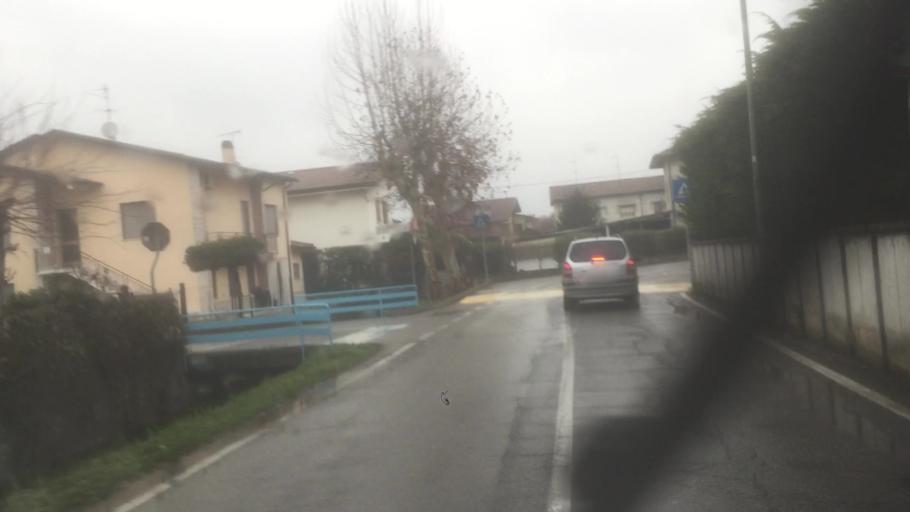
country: IT
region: Lombardy
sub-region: Provincia di Mantova
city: Castel Goffredo
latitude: 45.2971
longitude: 10.4709
